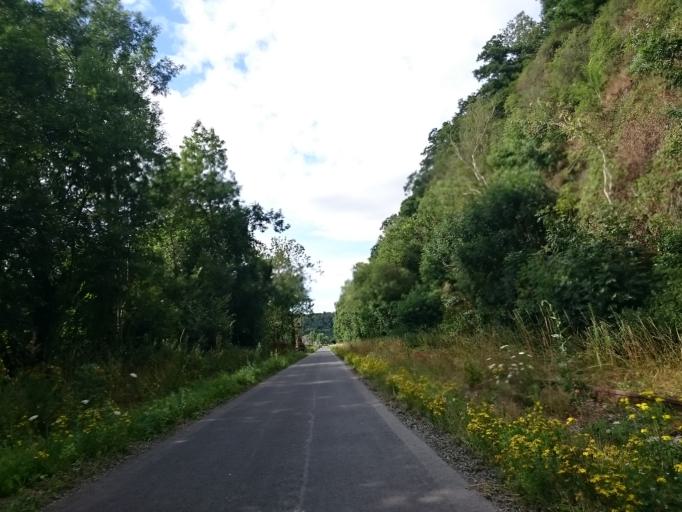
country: FR
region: Lower Normandy
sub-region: Departement du Calvados
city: Thury-Harcourt
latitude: 49.0301
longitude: -0.4649
